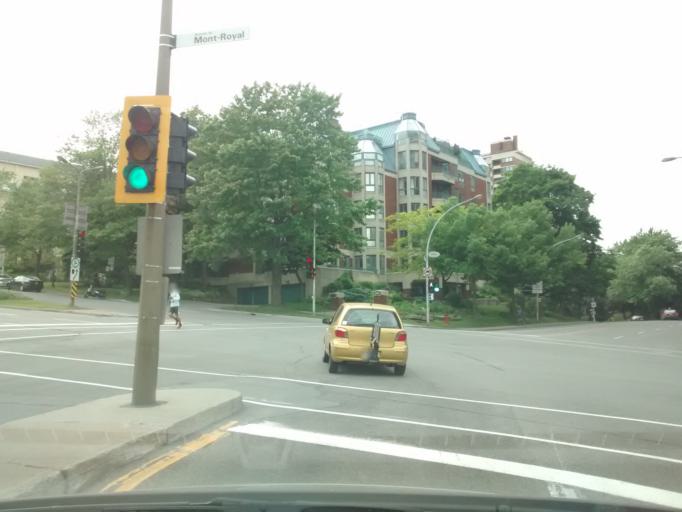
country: CA
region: Quebec
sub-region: Montreal
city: Montreal
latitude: 45.5158
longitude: -73.5899
